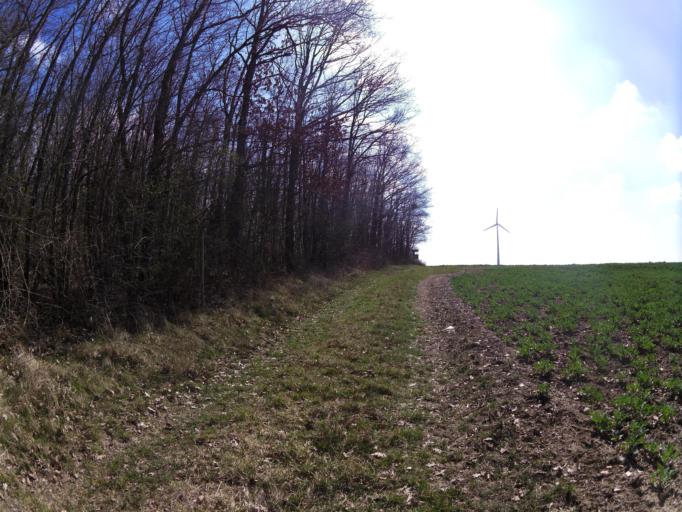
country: DE
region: Bavaria
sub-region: Regierungsbezirk Unterfranken
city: Nordheim
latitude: 49.8406
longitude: 10.1620
